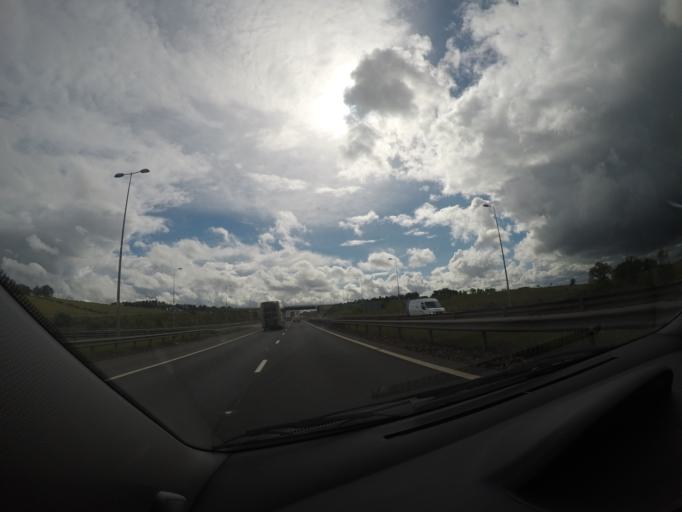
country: GB
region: Scotland
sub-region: North Lanarkshire
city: Glenboig
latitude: 55.9206
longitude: -4.0581
